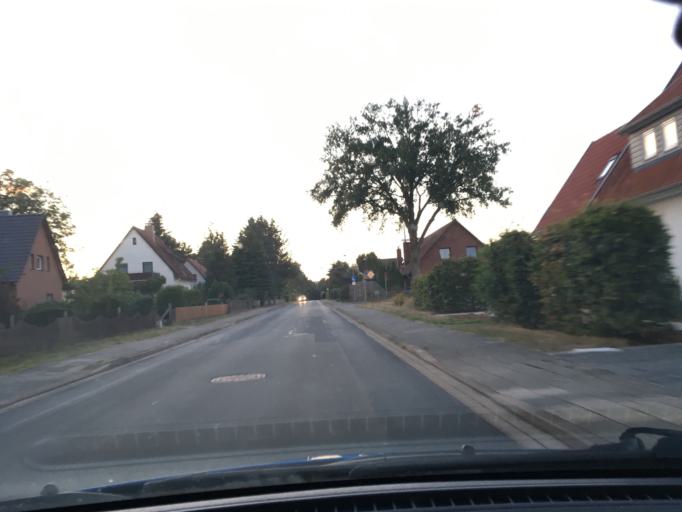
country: DE
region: Lower Saxony
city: Fassberg
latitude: 52.8982
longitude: 10.1595
